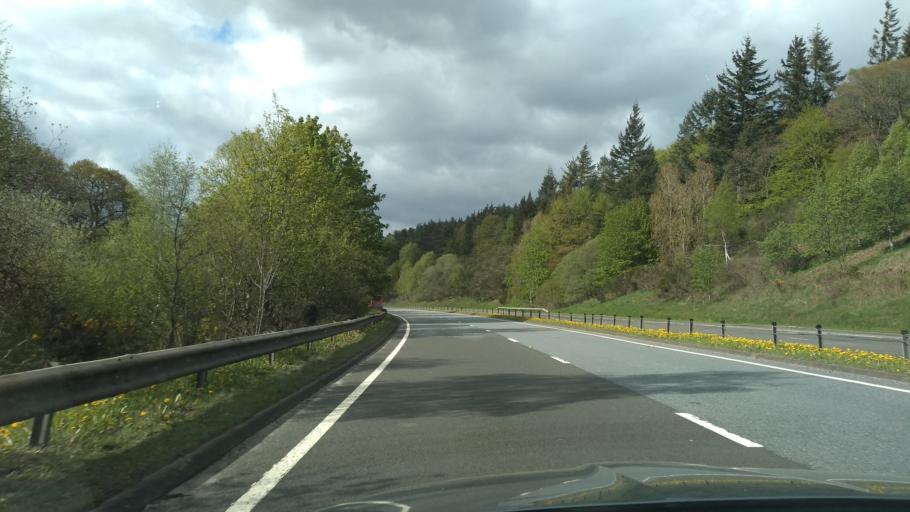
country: GB
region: Scotland
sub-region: Perth and Kinross
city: Pitlochry
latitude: 56.6640
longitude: -3.6722
